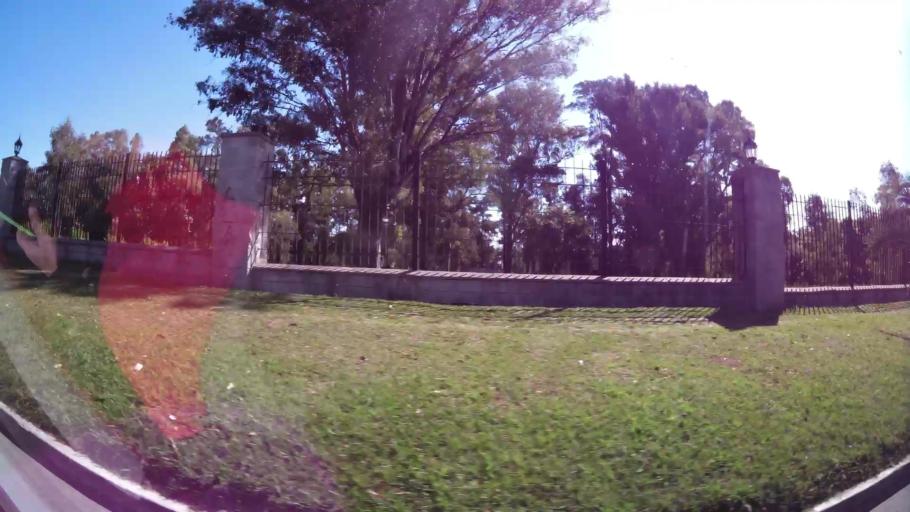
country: AR
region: Buenos Aires
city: Santa Catalina - Dique Lujan
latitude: -34.4935
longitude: -58.6969
